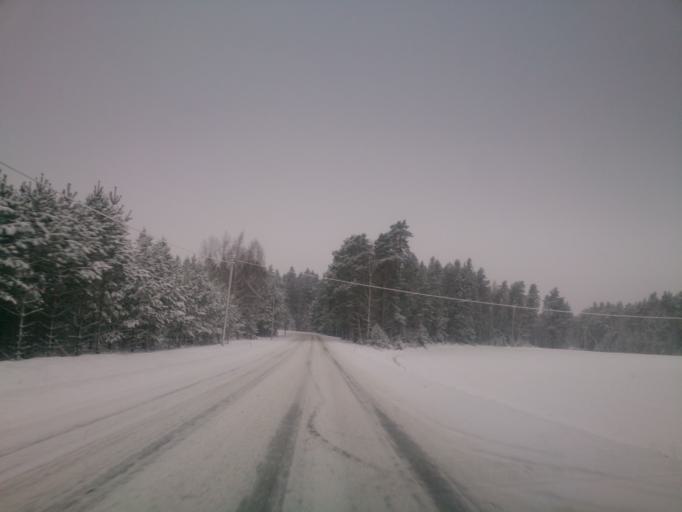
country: SE
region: OEstergoetland
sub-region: Finspangs Kommun
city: Finspang
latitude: 58.6579
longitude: 15.8003
